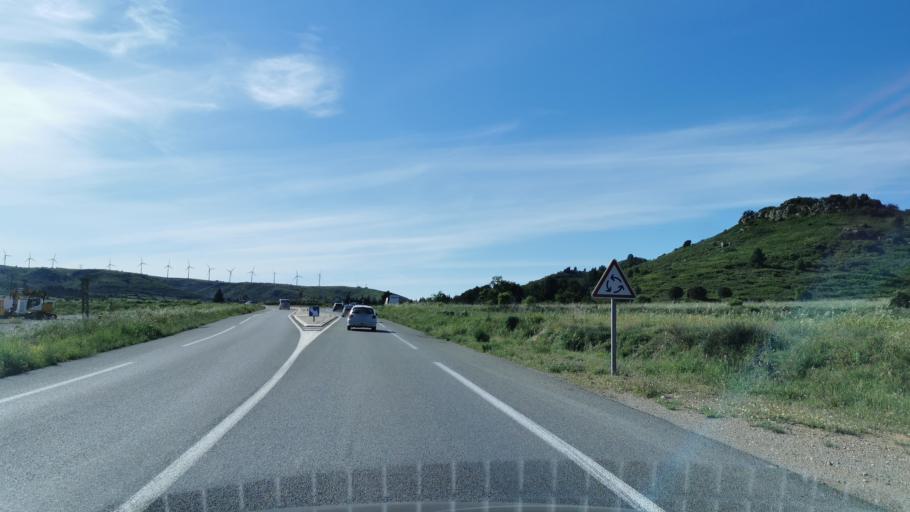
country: FR
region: Languedoc-Roussillon
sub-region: Departement de l'Aude
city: Nevian
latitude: 43.1902
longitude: 2.9111
